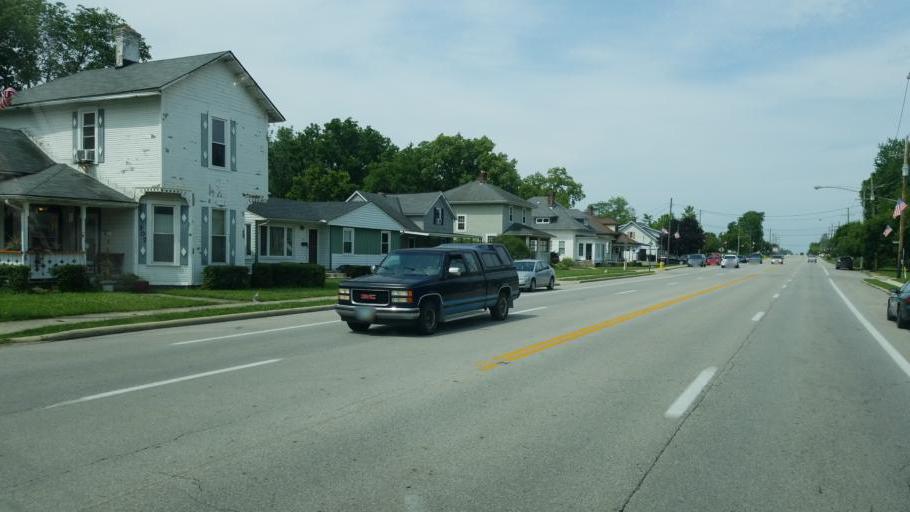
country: US
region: Ohio
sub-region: Madison County
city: West Jefferson
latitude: 39.9445
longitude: -83.2766
